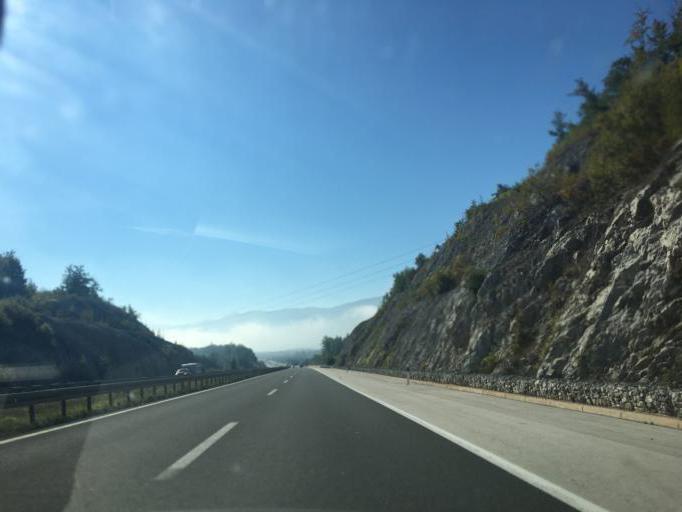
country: HR
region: Zadarska
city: Obrovac
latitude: 44.3591
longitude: 15.6400
